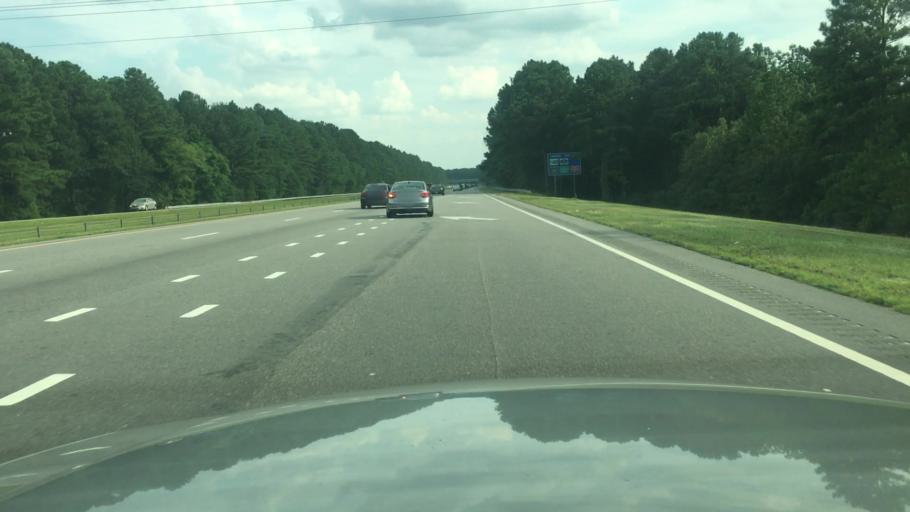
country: US
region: North Carolina
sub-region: Cumberland County
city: Fort Bragg
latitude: 35.0937
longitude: -78.9679
